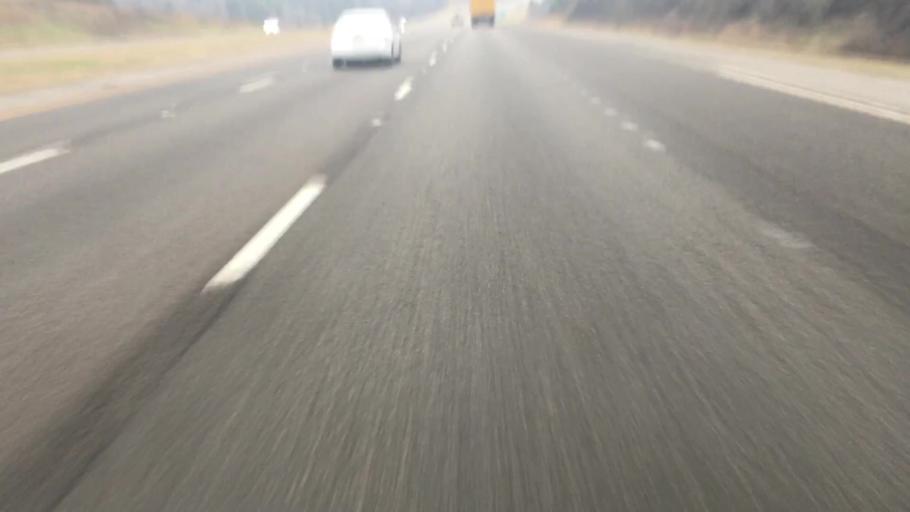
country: US
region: Alabama
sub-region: Jefferson County
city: Adamsville
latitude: 33.6150
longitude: -86.9348
